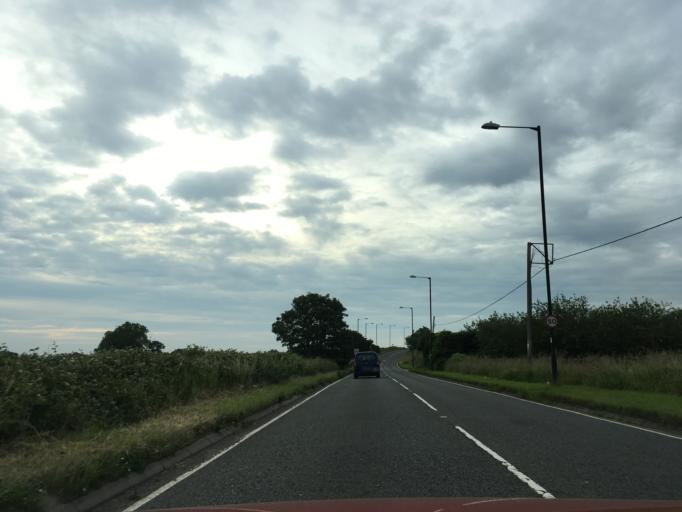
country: GB
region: England
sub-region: North Somerset
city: Easton-in-Gordano
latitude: 51.4709
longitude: -2.6885
